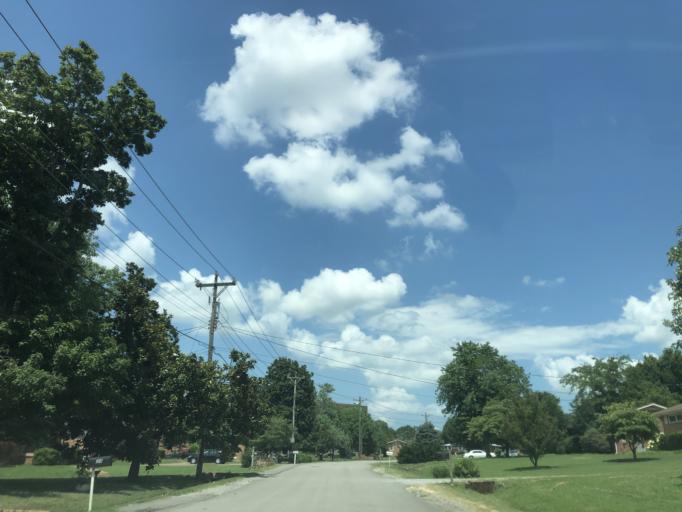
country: US
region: Tennessee
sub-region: Davidson County
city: Lakewood
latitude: 36.2020
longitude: -86.6153
